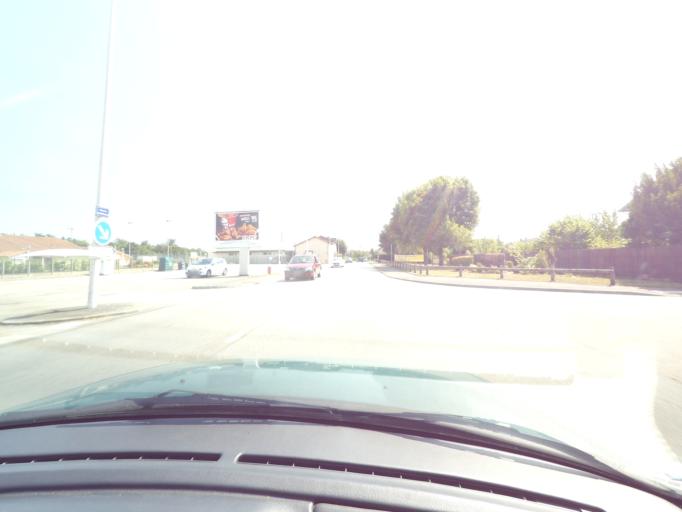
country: FR
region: Limousin
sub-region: Departement de la Haute-Vienne
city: Feytiat
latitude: 45.8132
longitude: 1.3342
